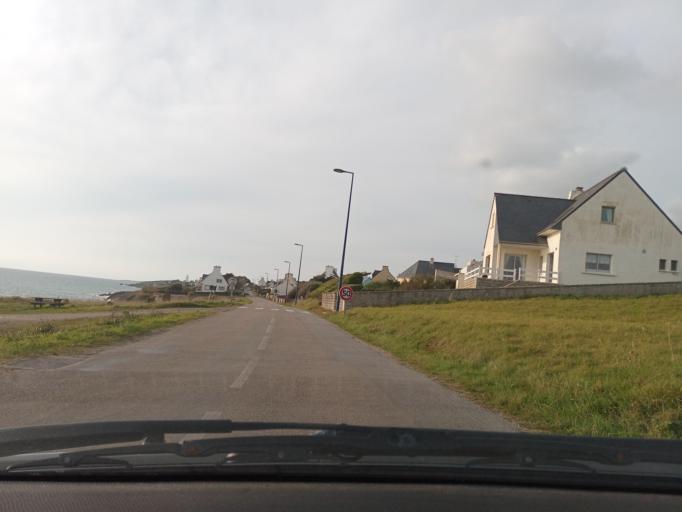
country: FR
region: Brittany
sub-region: Departement du Finistere
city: Plozevet
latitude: 47.9813
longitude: -4.4501
